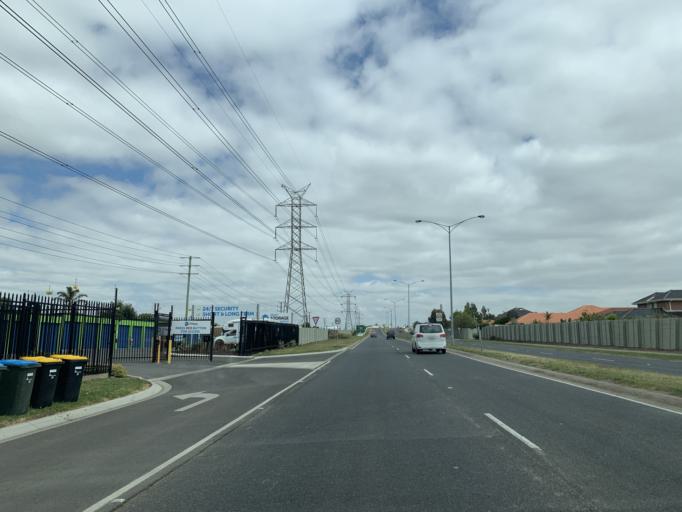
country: AU
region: Victoria
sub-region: Moonee Valley
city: Keilor East
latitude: -37.7406
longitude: 144.8589
